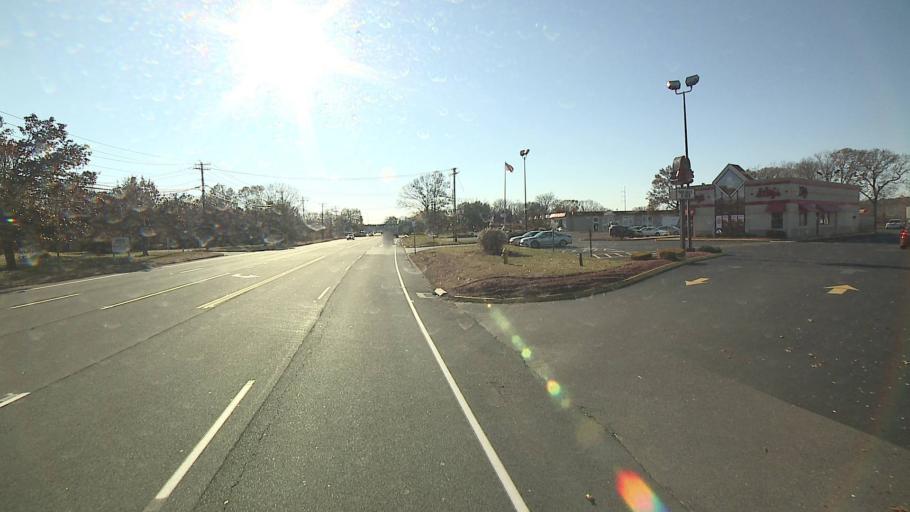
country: US
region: Connecticut
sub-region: New Haven County
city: North Haven
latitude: 41.4020
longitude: -72.8490
